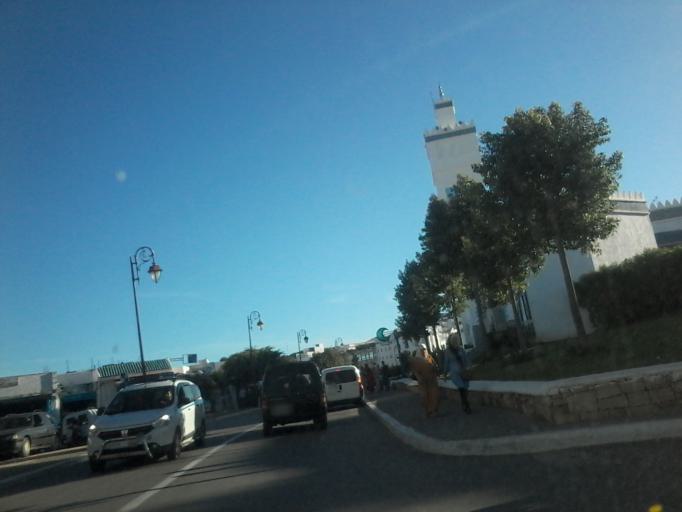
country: MA
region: Tanger-Tetouan
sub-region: Tetouan
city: Martil
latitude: 35.6899
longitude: -5.3301
